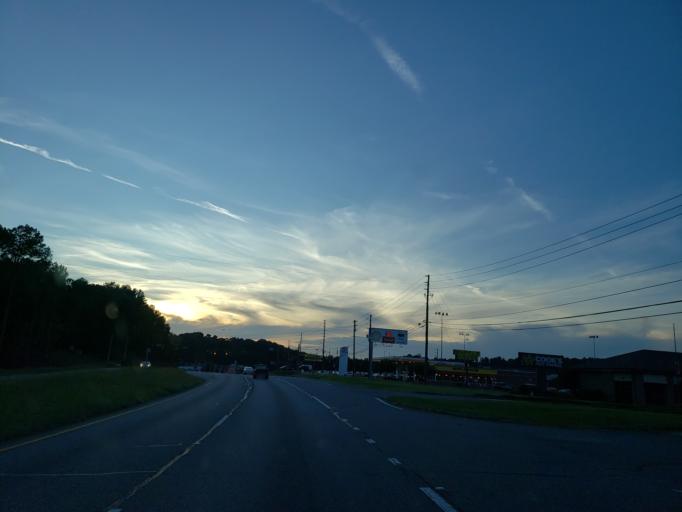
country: US
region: Georgia
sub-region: Floyd County
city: Rome
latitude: 34.2224
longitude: -85.1475
